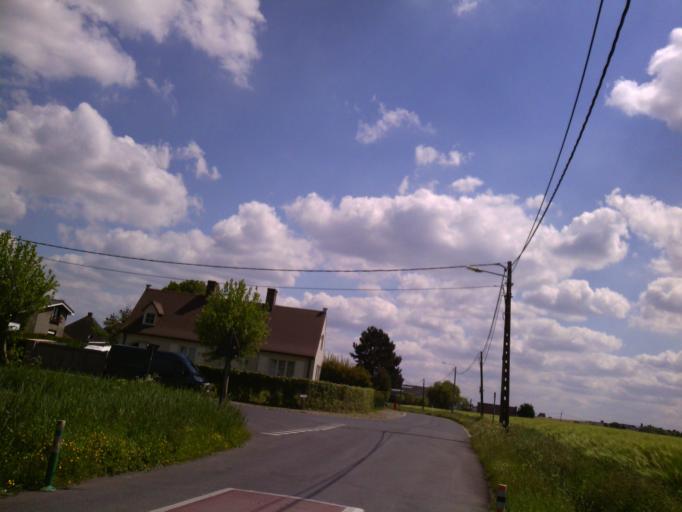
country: BE
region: Flanders
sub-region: Provincie West-Vlaanderen
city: Wevelgem
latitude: 50.7843
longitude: 3.1573
